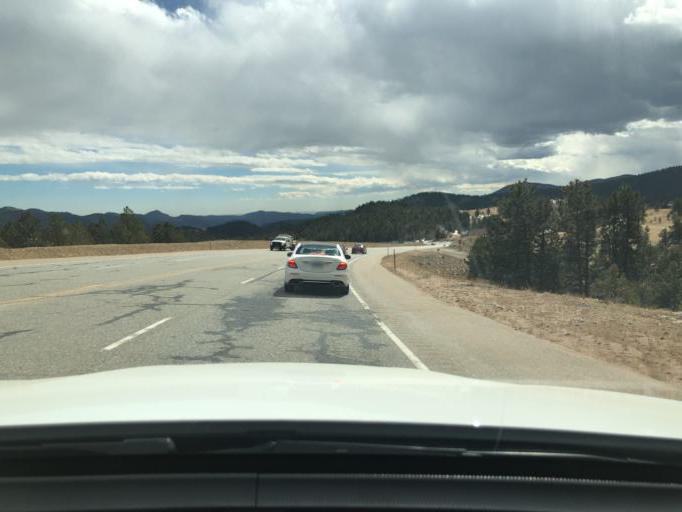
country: US
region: Colorado
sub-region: Gilpin County
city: Central City
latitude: 39.7888
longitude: -105.4987
